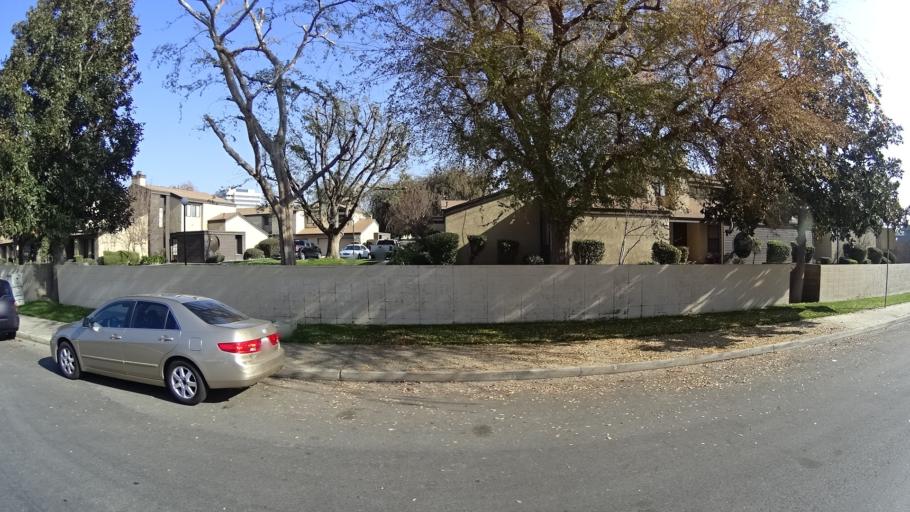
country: US
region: California
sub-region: Kern County
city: Bakersfield
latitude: 35.3606
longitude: -119.0648
